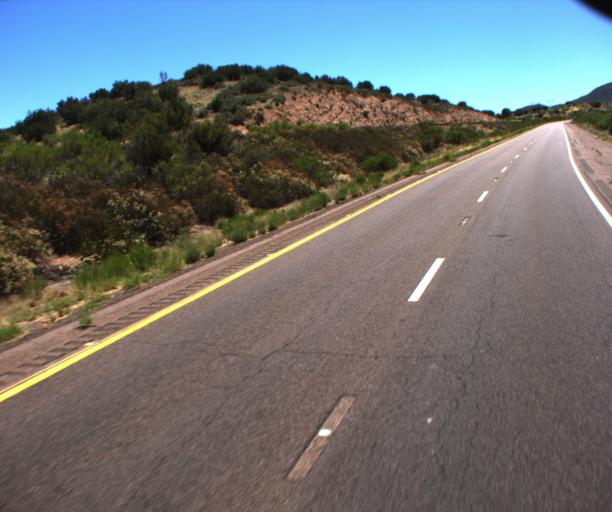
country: US
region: Arizona
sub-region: Gila County
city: Tonto Basin
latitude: 33.9992
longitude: -111.3613
